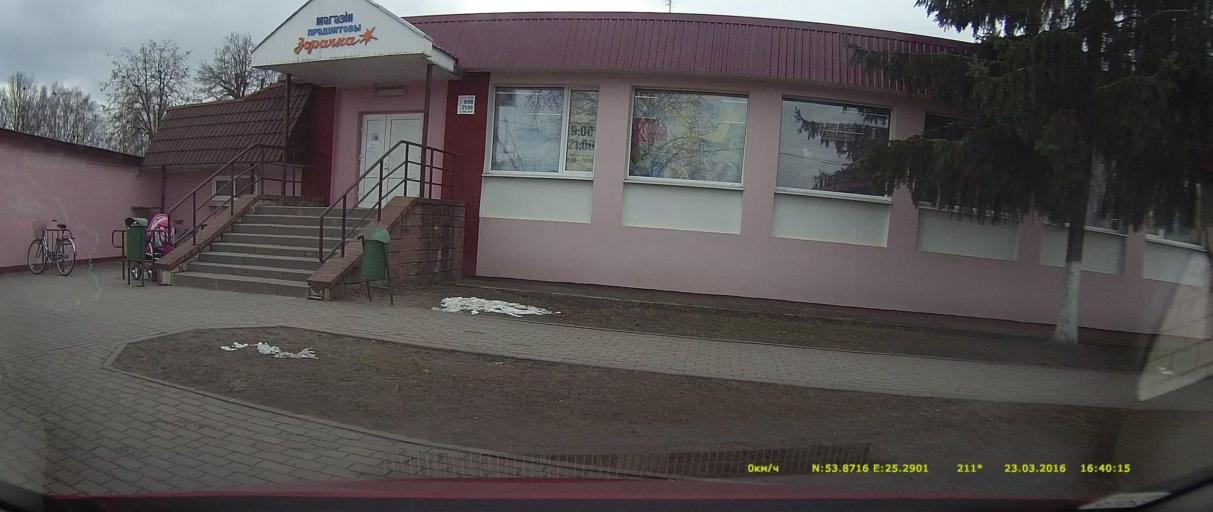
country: BY
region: Grodnenskaya
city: Lida
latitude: 53.8792
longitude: 25.2858
